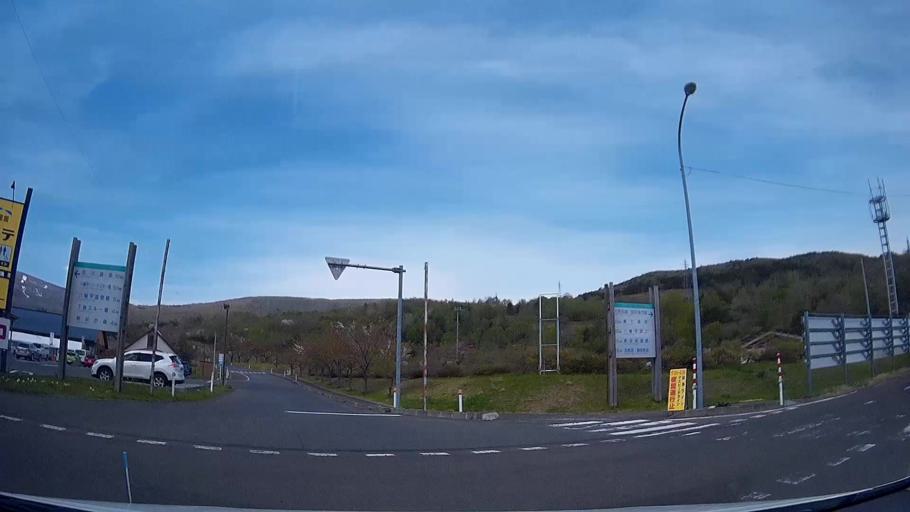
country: JP
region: Iwate
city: Shizukuishi
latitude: 39.9209
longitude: 140.9760
